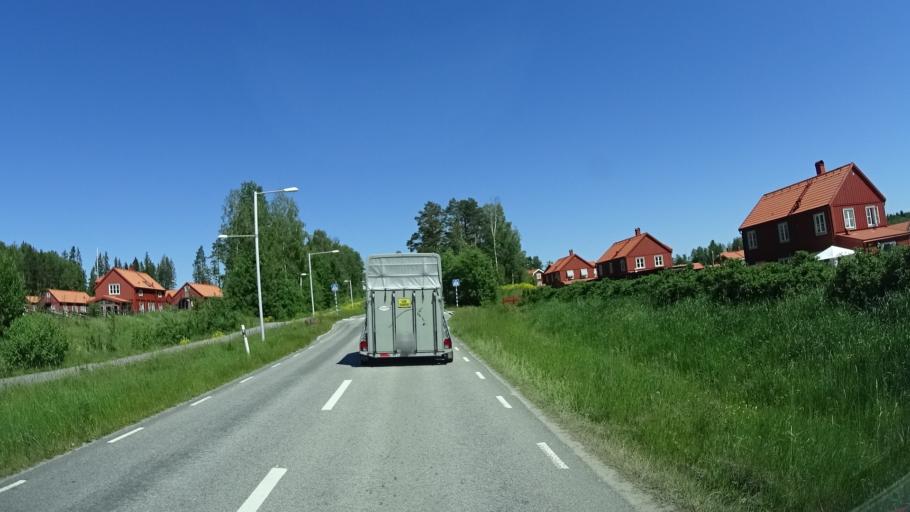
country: SE
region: Stockholm
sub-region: Vallentuna Kommun
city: Vallentuna
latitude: 59.5791
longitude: 18.0987
